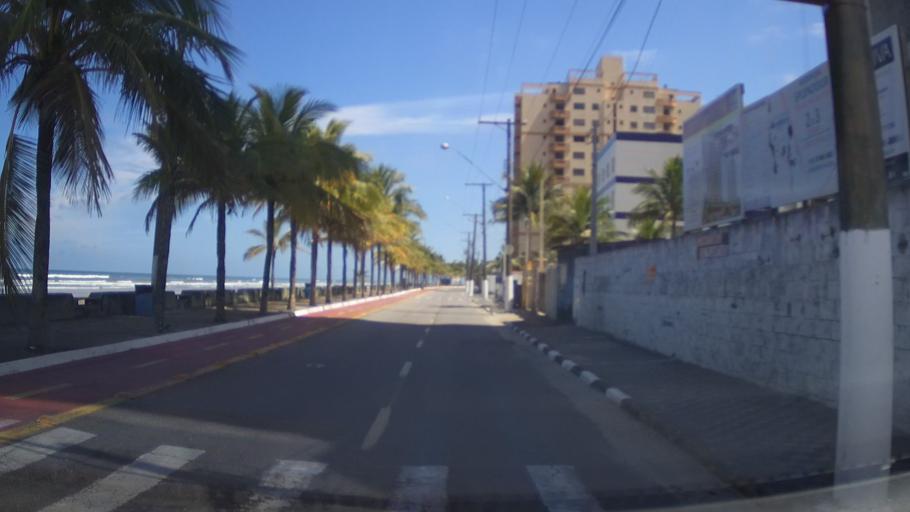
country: BR
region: Sao Paulo
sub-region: Mongagua
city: Mongagua
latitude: -24.0904
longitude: -46.6083
